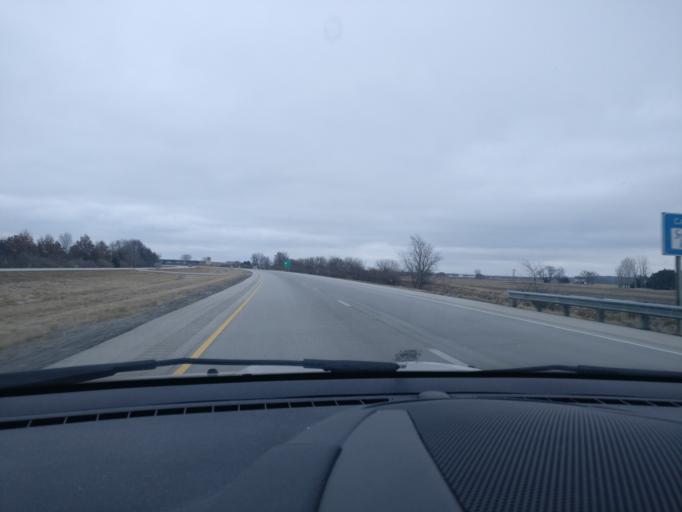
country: US
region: Illinois
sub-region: Rock Island County
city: Port Byron
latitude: 41.5437
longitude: -90.2609
